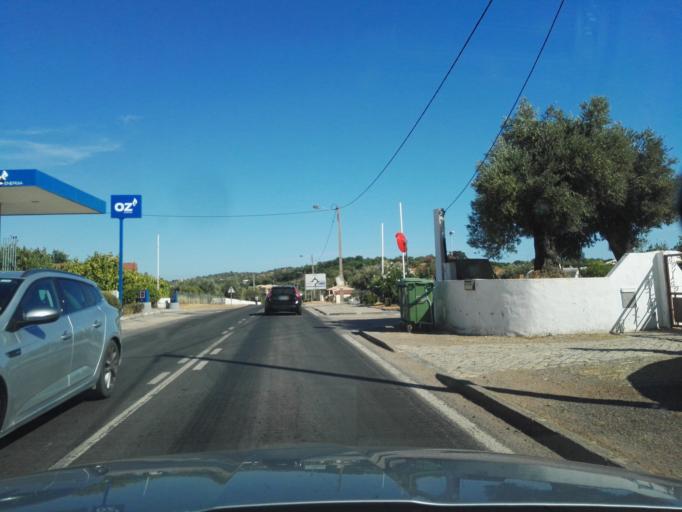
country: PT
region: Faro
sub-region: Olhao
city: Moncarapacho
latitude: 37.1532
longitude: -7.7920
